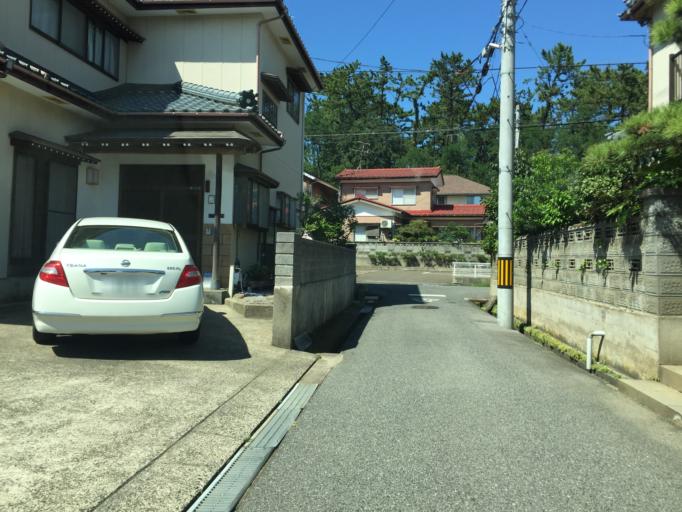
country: JP
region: Niigata
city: Niigata-shi
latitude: 37.9038
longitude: 139.0011
